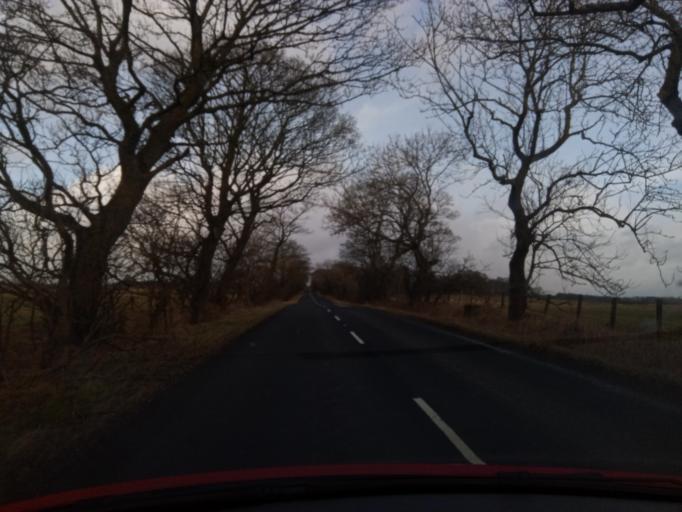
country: GB
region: England
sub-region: Northumberland
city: Acomb
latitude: 55.0918
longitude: -2.0555
